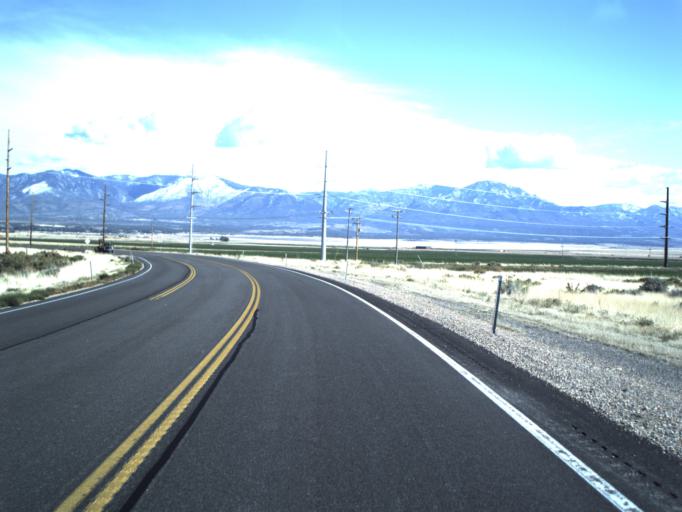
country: US
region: Utah
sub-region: Millard County
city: Fillmore
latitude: 39.1189
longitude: -112.3548
